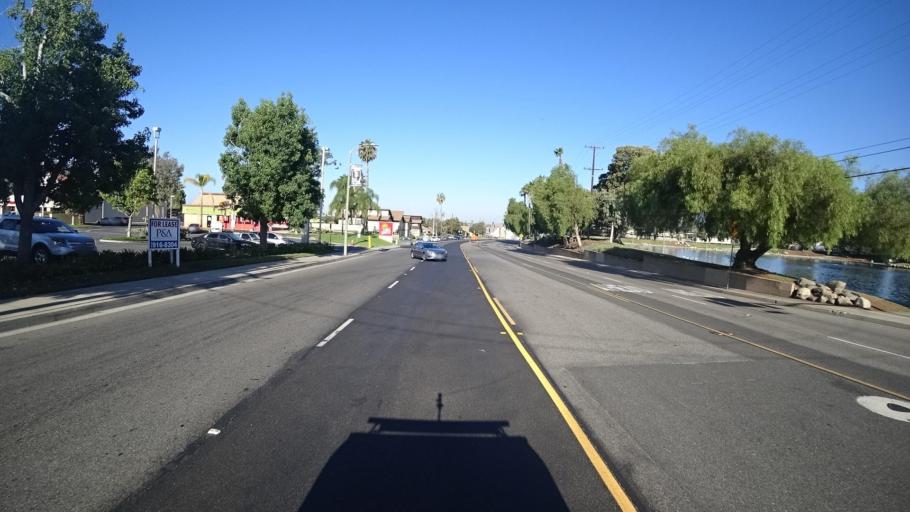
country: US
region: California
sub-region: Orange County
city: Villa Park
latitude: 33.8345
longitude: -117.8376
